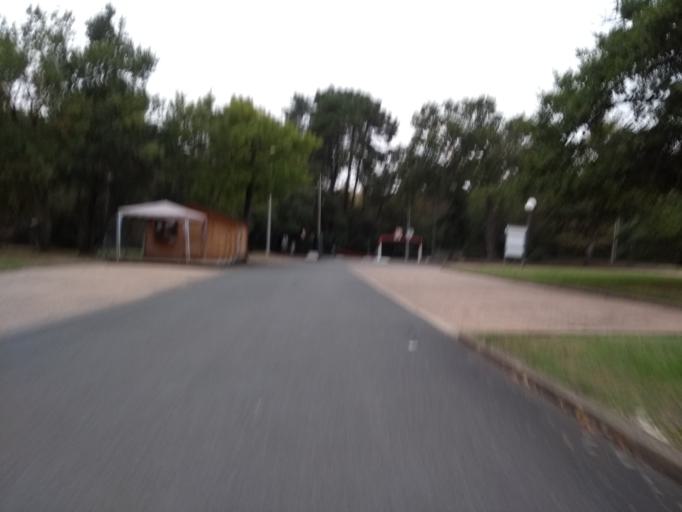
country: FR
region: Aquitaine
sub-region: Departement de la Gironde
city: Talence
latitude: 44.7928
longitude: -0.5984
